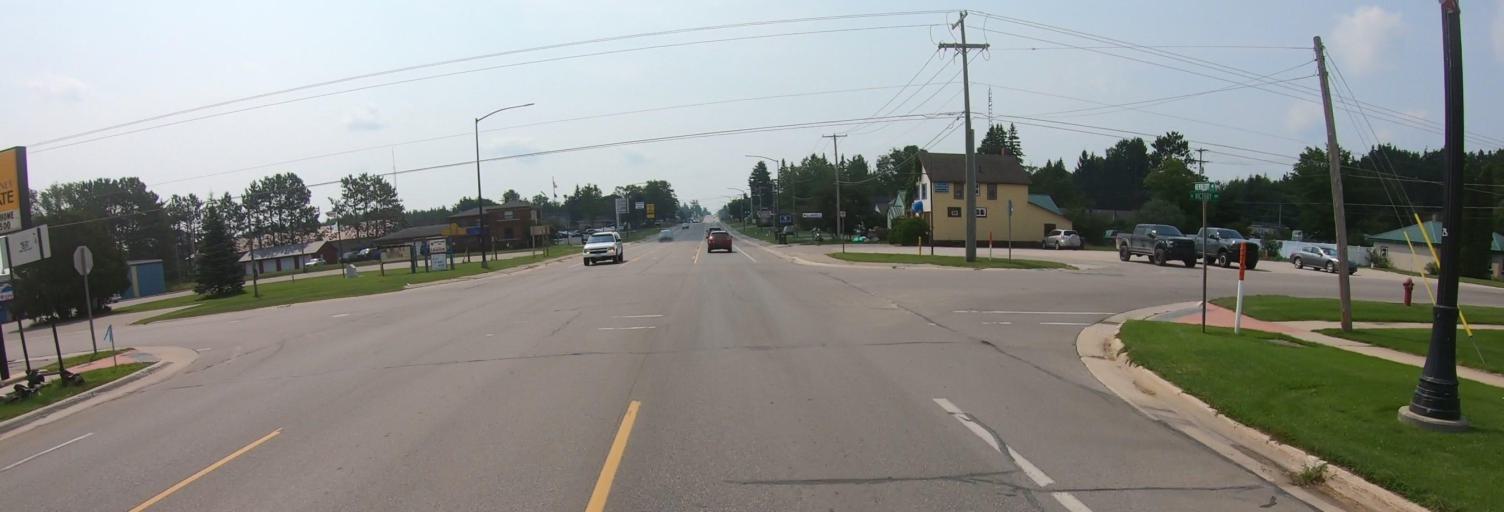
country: US
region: Michigan
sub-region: Luce County
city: Newberry
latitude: 46.3468
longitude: -85.5099
